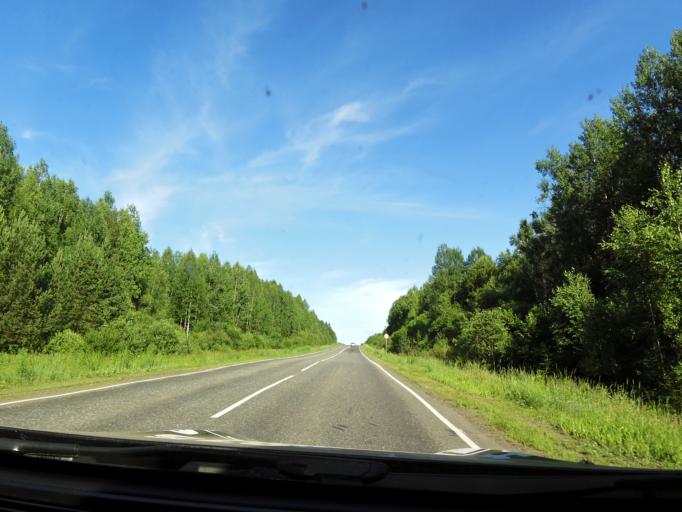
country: RU
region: Kirov
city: Chernaya Kholunitsa
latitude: 58.8888
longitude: 51.3681
